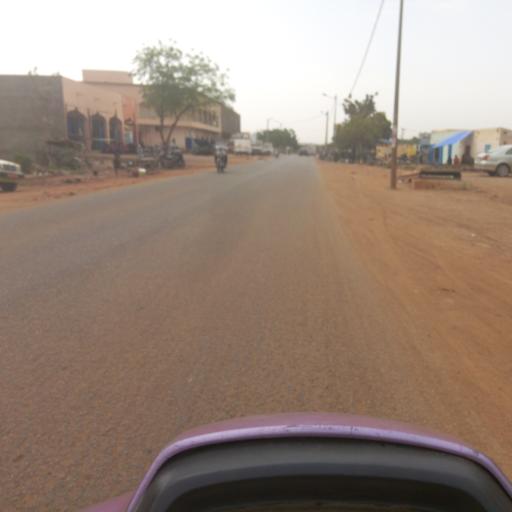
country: ML
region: Bamako
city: Bamako
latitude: 12.6551
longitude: -7.9363
